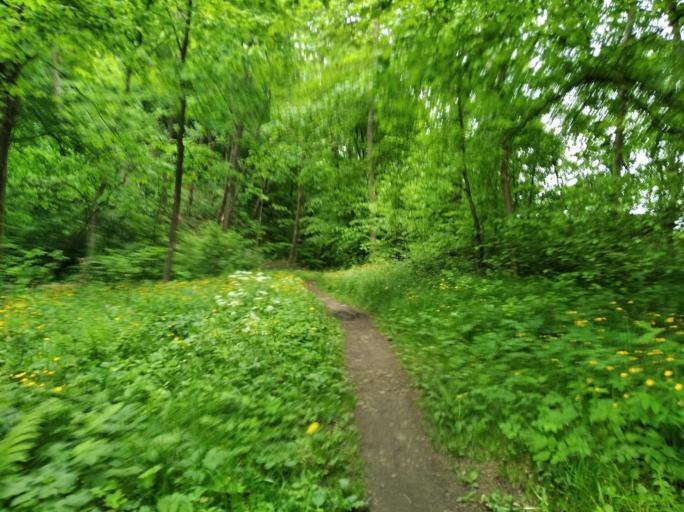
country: PL
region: Subcarpathian Voivodeship
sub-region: Powiat strzyzowski
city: Czudec
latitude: 49.9379
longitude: 21.8364
